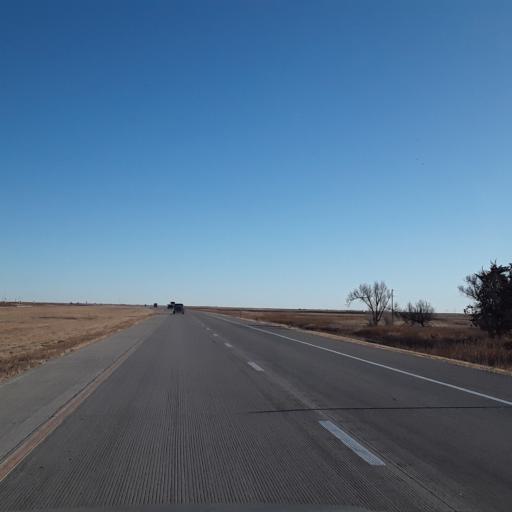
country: US
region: Kansas
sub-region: Seward County
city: Liberal
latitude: 37.0983
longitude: -100.8058
